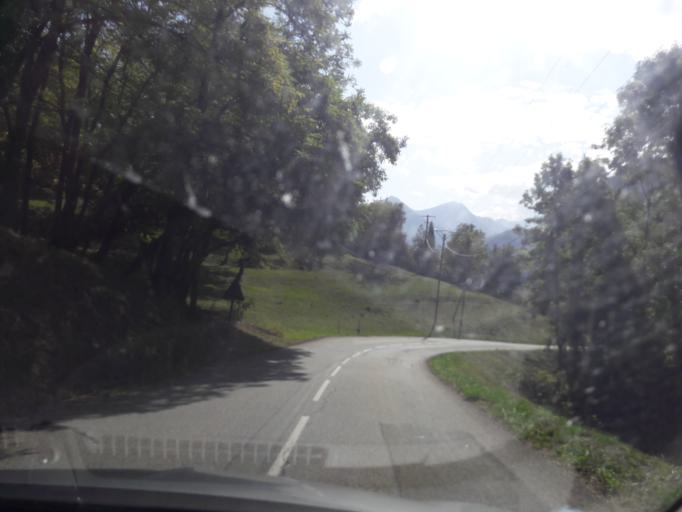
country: FR
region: Rhone-Alpes
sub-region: Departement de la Savoie
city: Saint-Jean-de-Maurienne
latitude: 45.3158
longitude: 6.3495
